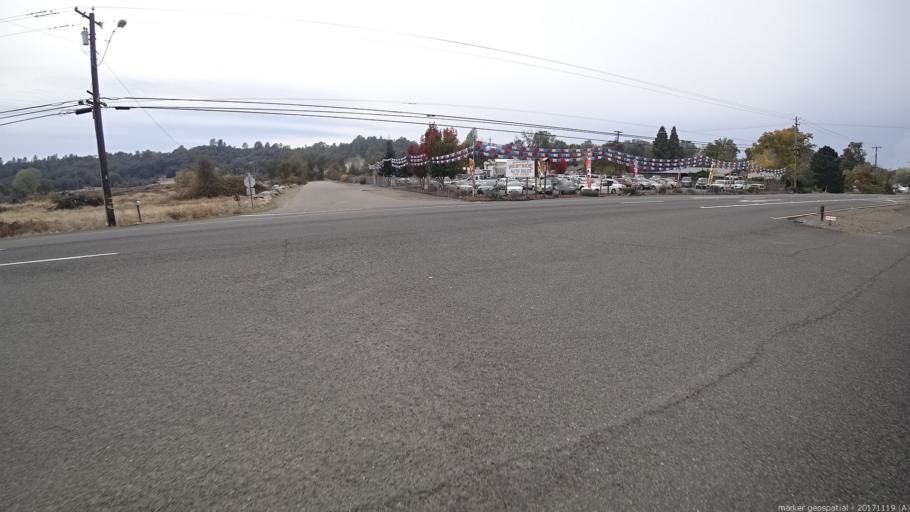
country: US
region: California
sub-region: Shasta County
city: Anderson
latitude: 40.4812
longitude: -122.3463
